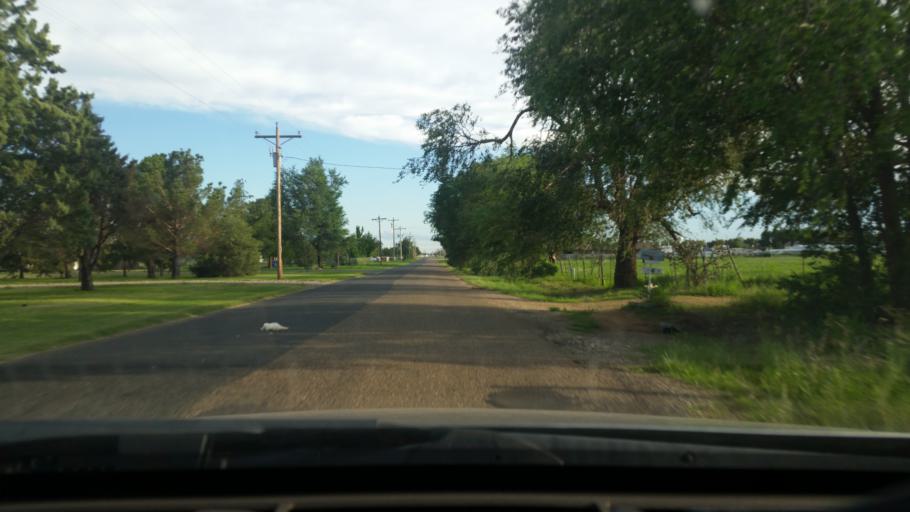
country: US
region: New Mexico
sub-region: Curry County
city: Clovis
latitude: 34.4528
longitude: -103.1784
